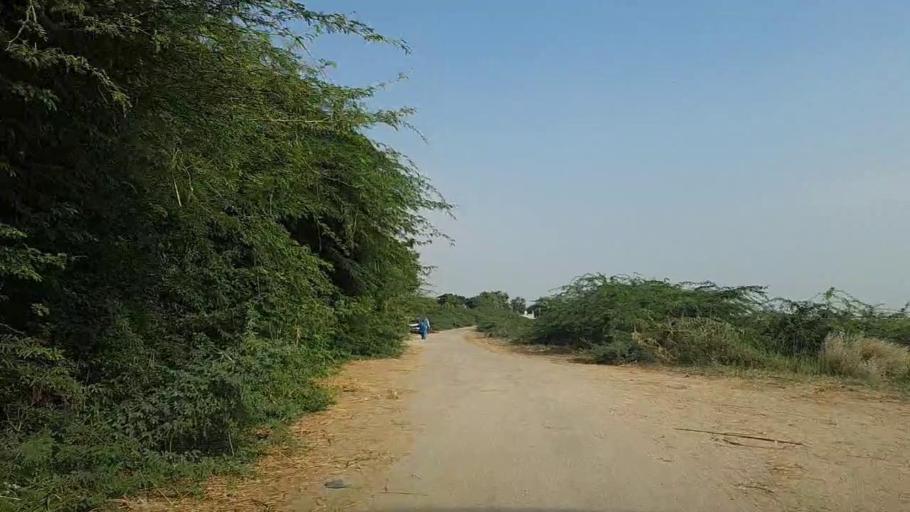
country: PK
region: Sindh
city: Thatta
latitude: 24.6520
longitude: 67.9176
